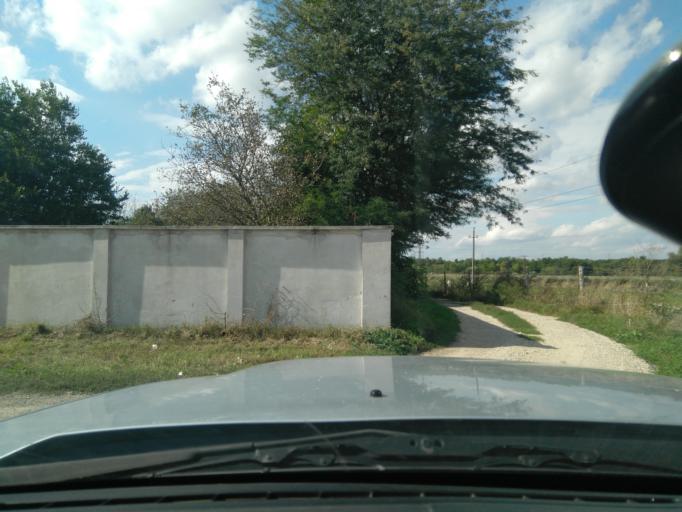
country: HU
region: Fejer
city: Bicske
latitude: 47.4851
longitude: 18.6553
